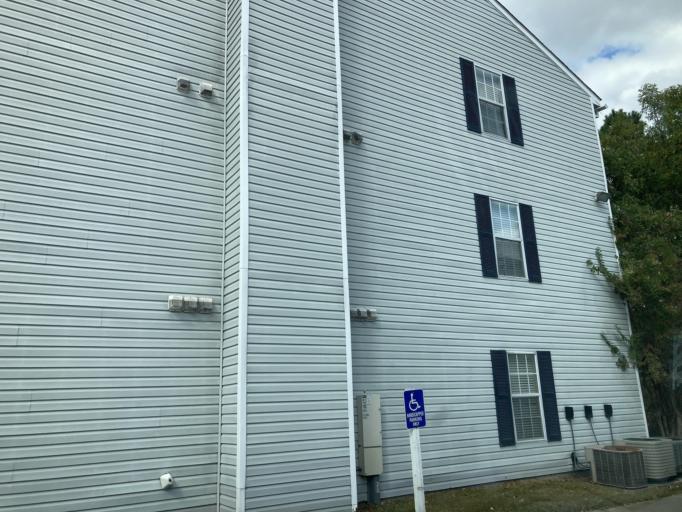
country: US
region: Mississippi
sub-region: Lamar County
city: Arnold Line
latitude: 31.3301
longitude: -89.3544
